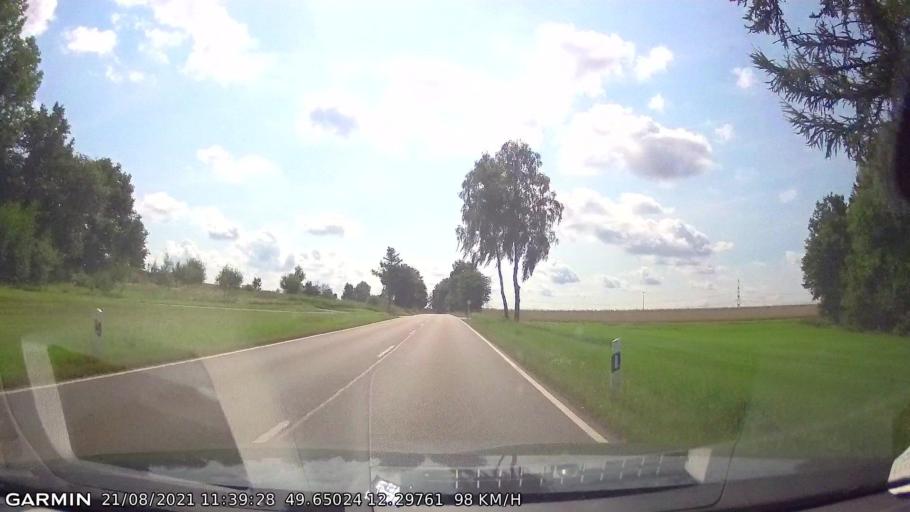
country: DE
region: Bavaria
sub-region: Upper Palatinate
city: Waldthurn
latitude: 49.6502
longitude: 12.2976
